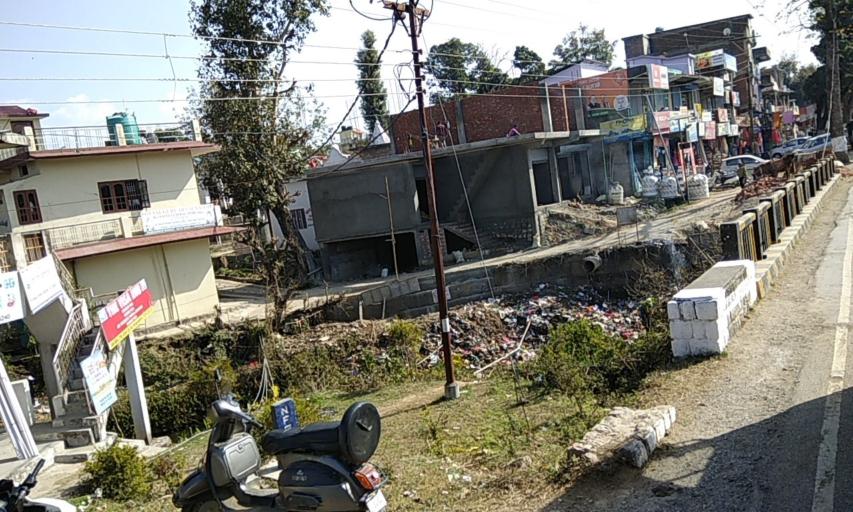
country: IN
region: Himachal Pradesh
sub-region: Kangra
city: Yol
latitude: 32.2149
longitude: 76.1811
